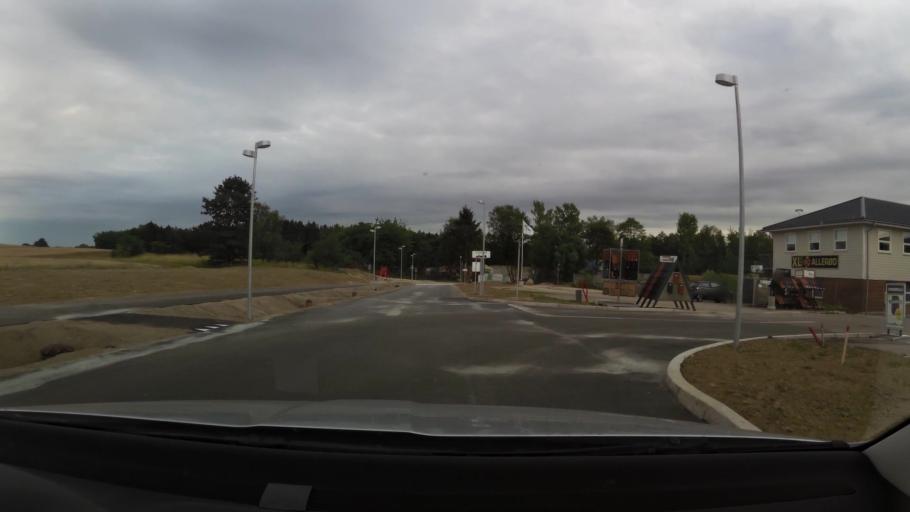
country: DK
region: Capital Region
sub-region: Allerod Kommune
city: Blovstrod
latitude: 55.8644
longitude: 12.3734
